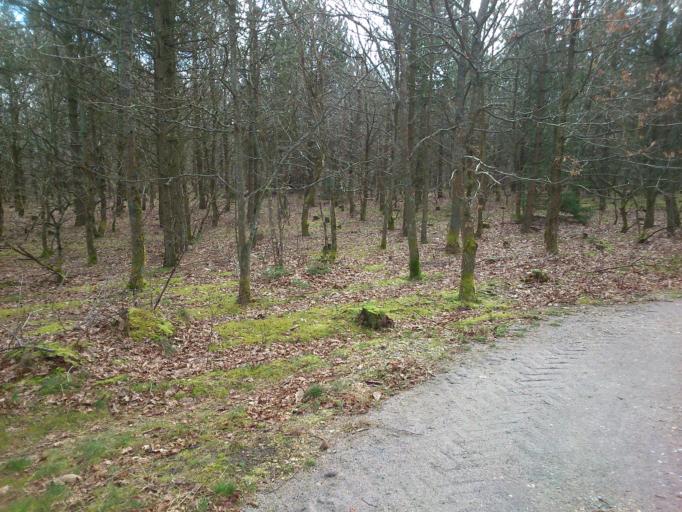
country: DK
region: Central Jutland
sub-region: Ringkobing-Skjern Kommune
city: Skjern
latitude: 55.9510
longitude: 8.5243
